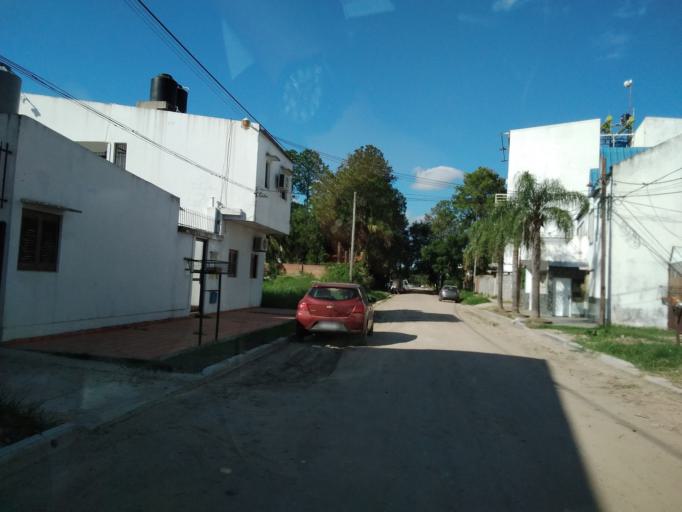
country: AR
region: Corrientes
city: Corrientes
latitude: -27.4651
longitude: -58.7872
